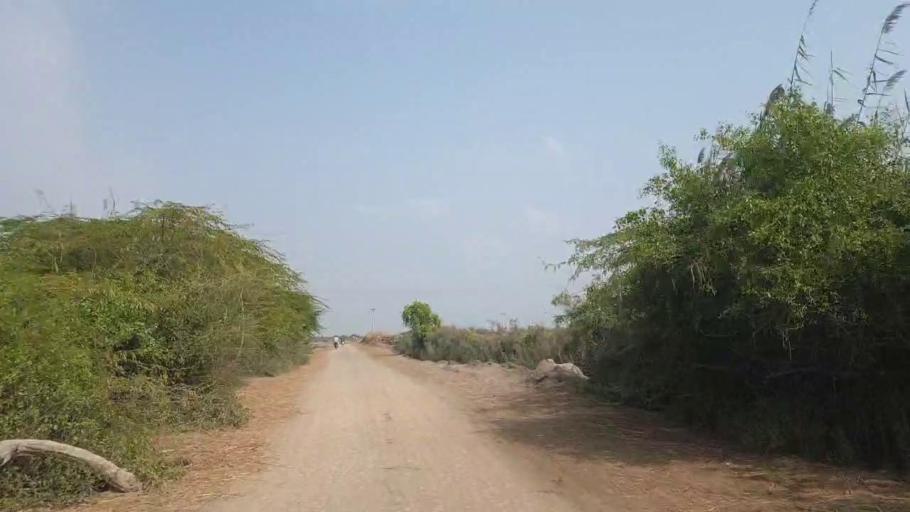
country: PK
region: Sindh
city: Badin
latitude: 24.5504
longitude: 68.7297
